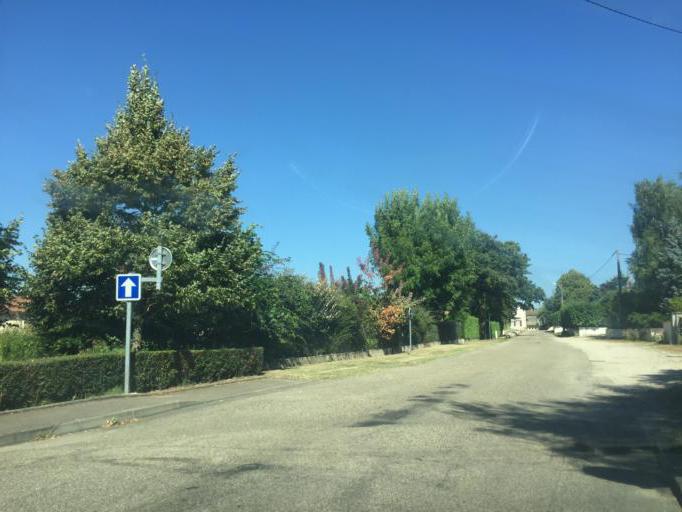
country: FR
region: Rhone-Alpes
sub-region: Departement de l'Ain
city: Tramoyes
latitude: 45.8747
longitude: 4.9683
